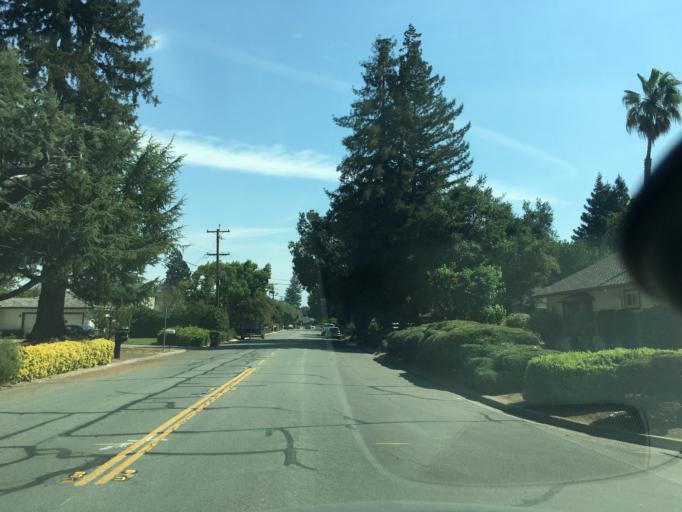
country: US
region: California
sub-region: Santa Clara County
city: Loyola
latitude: 37.3480
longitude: -122.0728
